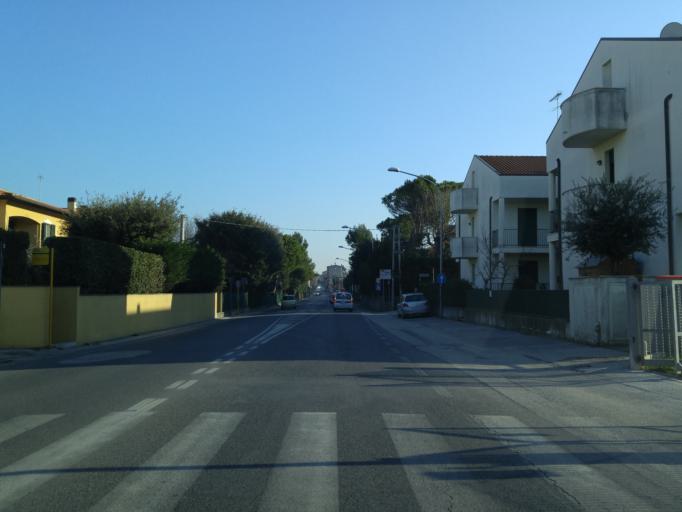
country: IT
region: The Marches
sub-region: Provincia di Pesaro e Urbino
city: Fano
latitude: 43.8501
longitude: 13.0073
